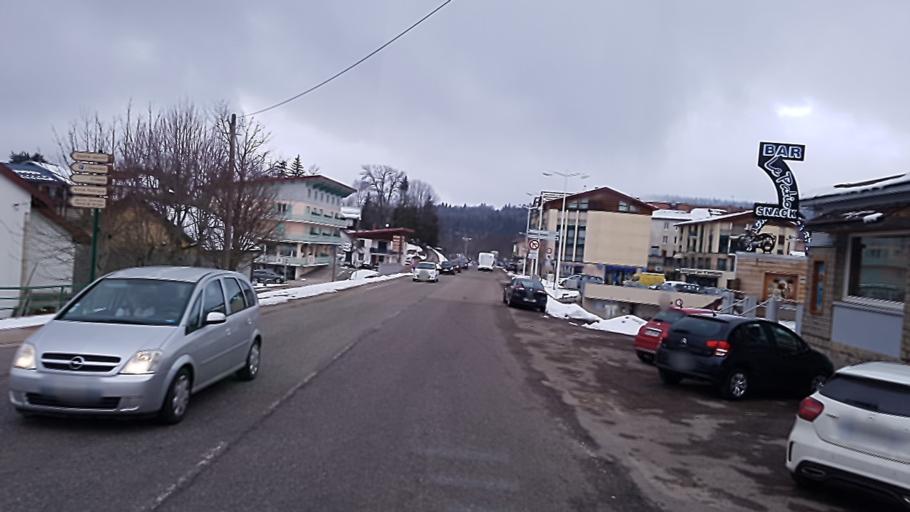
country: FR
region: Franche-Comte
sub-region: Departement du Jura
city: Les Rousses
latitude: 46.4842
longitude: 6.0599
